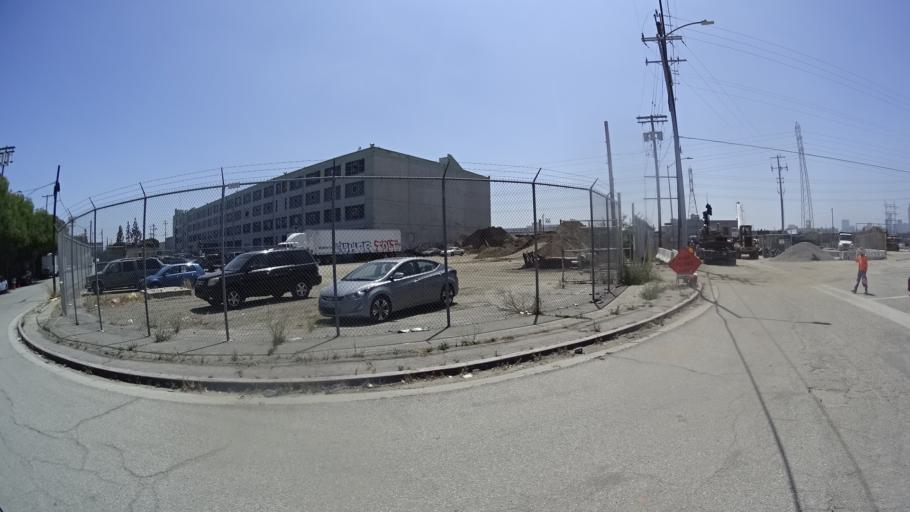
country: US
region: California
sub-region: Los Angeles County
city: Boyle Heights
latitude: 34.0365
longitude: -118.2254
